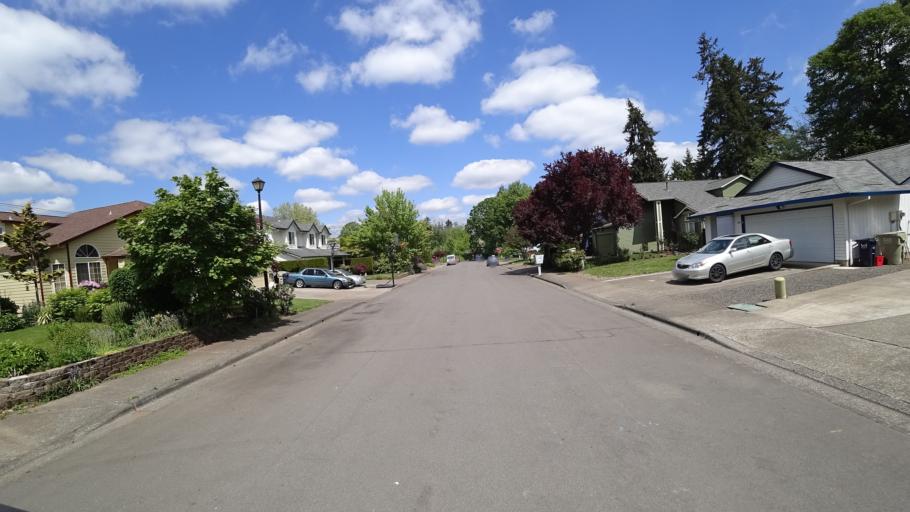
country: US
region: Oregon
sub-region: Washington County
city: Aloha
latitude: 45.5110
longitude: -122.8959
